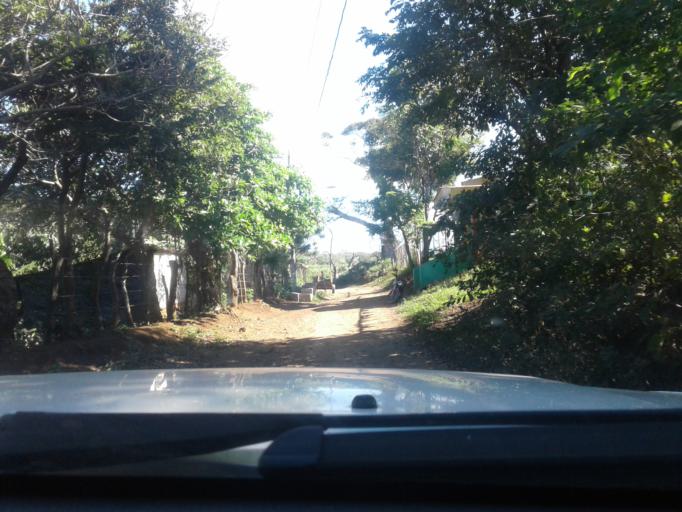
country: NI
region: Carazo
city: Santa Teresa
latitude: 11.7371
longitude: -86.1907
